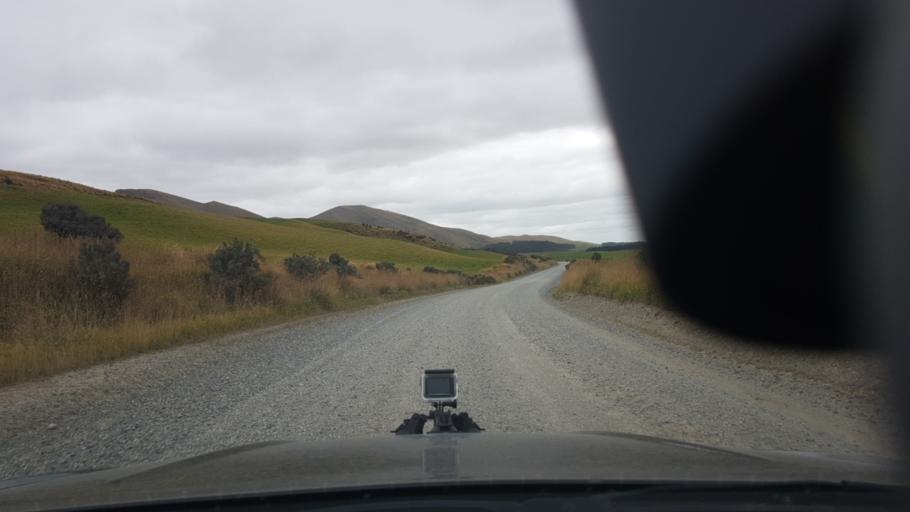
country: NZ
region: Otago
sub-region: Clutha District
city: Papatowai
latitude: -46.3256
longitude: 169.3846
